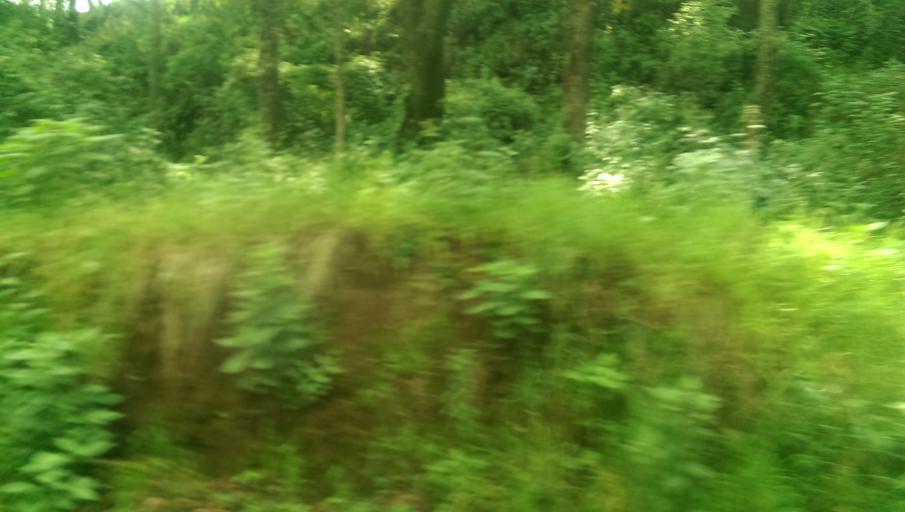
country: MX
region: Mexico
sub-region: Jilotepec
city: Jilotepec de Molina Enriquez
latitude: 19.9288
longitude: -99.4942
